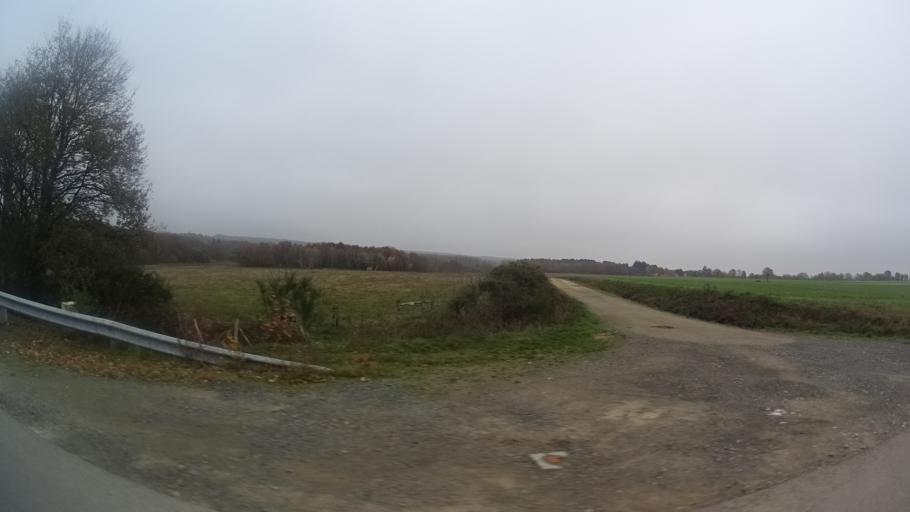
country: FR
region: Brittany
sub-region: Departement d'Ille-et-Vilaine
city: Sainte-Marie
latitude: 47.7073
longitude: -1.9935
